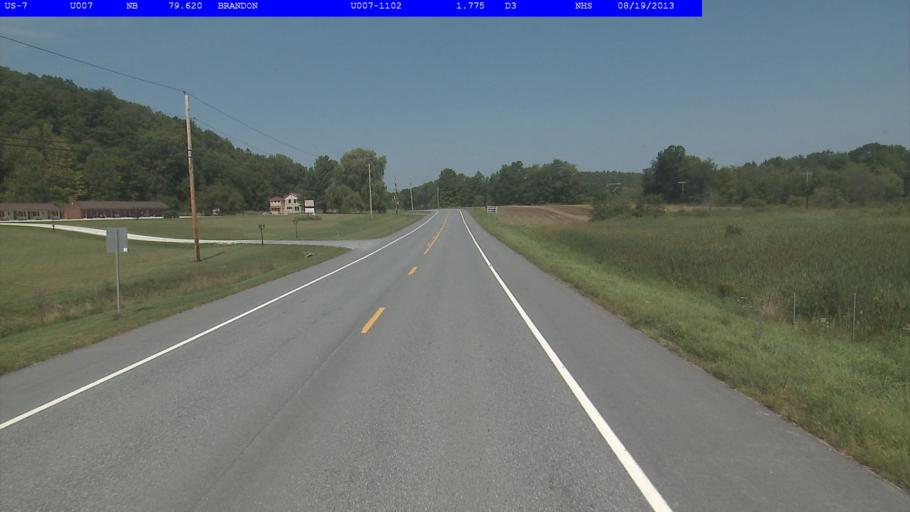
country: US
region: Vermont
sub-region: Rutland County
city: Brandon
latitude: 43.7787
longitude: -73.0571
